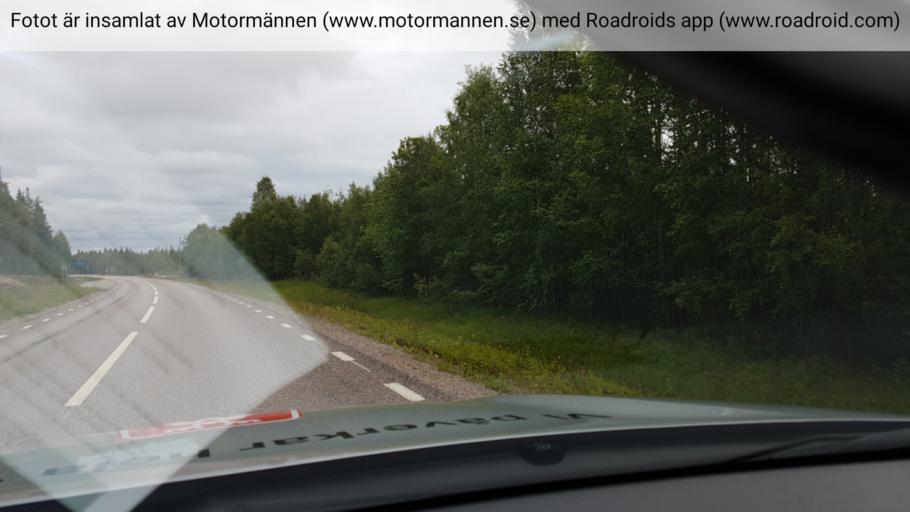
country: SE
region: Norrbotten
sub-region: Gallivare Kommun
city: Gaellivare
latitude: 67.0545
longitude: 21.2326
